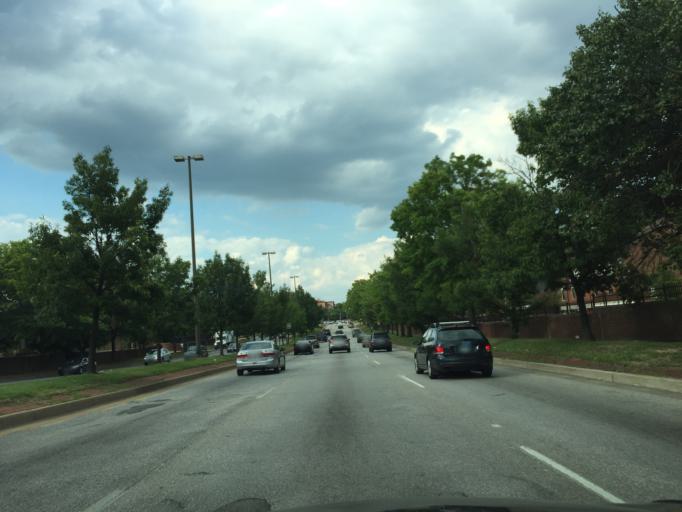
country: US
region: Maryland
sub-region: City of Baltimore
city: Baltimore
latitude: 39.2968
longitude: -76.6260
